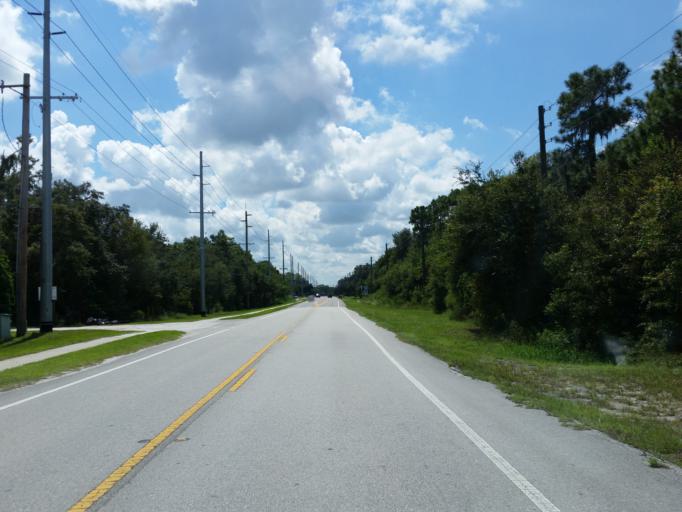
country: US
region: Florida
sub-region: Hillsborough County
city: Riverview
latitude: 27.8412
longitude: -82.3020
